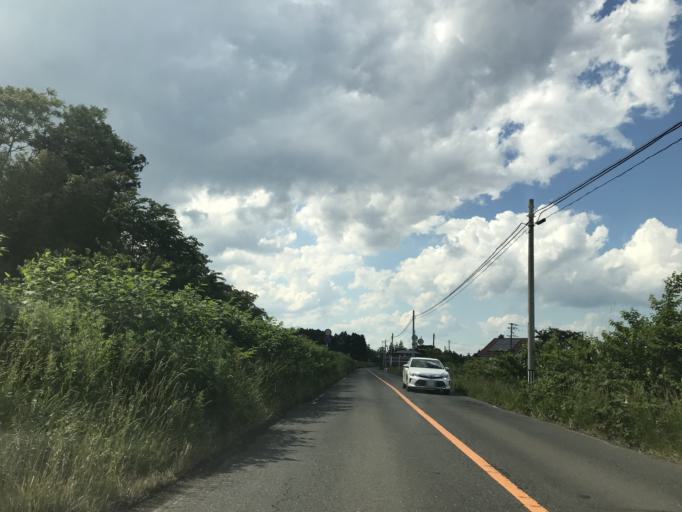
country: JP
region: Miyagi
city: Wakuya
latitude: 38.6534
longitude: 141.2146
